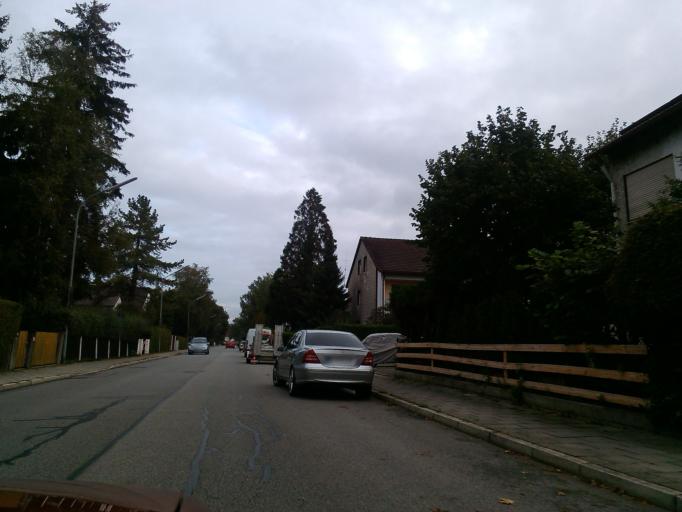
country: DE
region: Bavaria
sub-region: Upper Bavaria
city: Grobenzell
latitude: 48.1881
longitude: 11.3715
